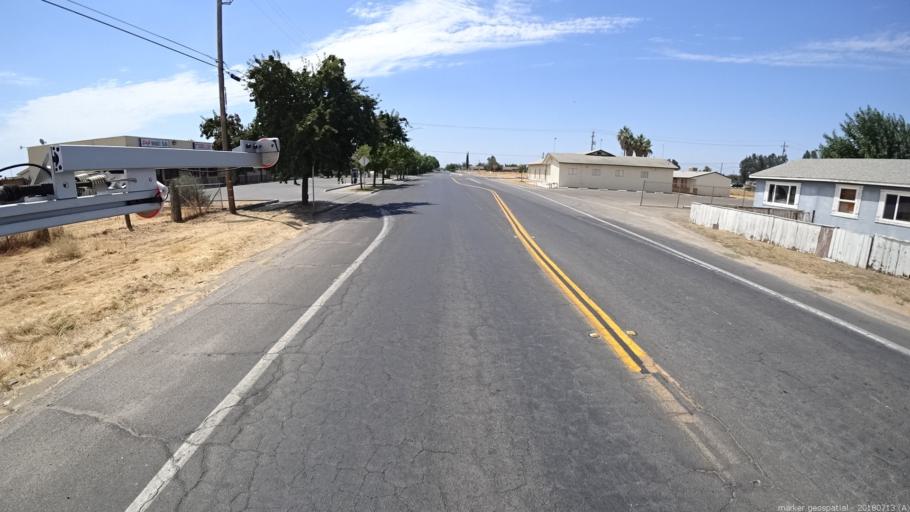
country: US
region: California
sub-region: Madera County
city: Madera
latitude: 36.9877
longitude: -120.0562
